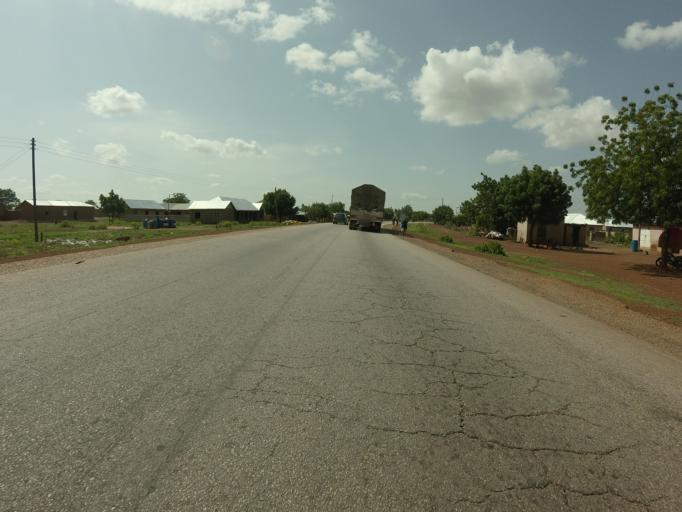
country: GH
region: Northern
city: Savelugu
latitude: 9.8742
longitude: -0.8722
